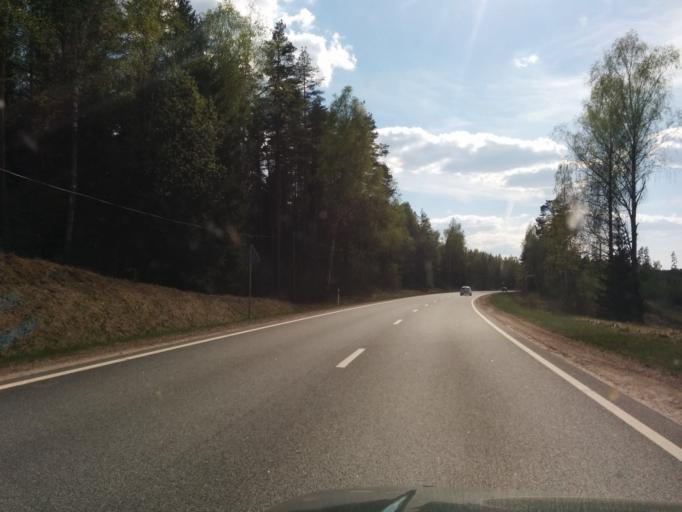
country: LV
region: Sigulda
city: Sigulda
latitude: 57.2804
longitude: 24.9084
